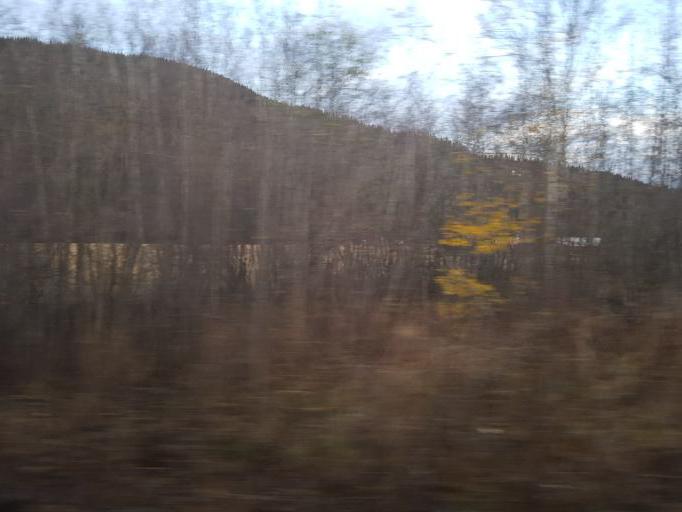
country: NO
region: Sor-Trondelag
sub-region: Melhus
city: Lundamo
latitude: 63.1544
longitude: 10.2881
